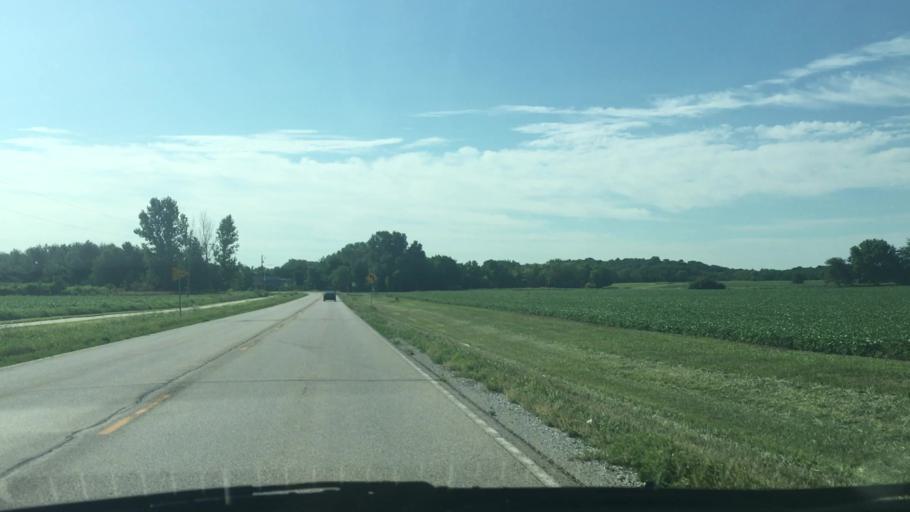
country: US
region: Iowa
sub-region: Johnson County
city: North Liberty
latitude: 41.7360
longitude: -91.5825
